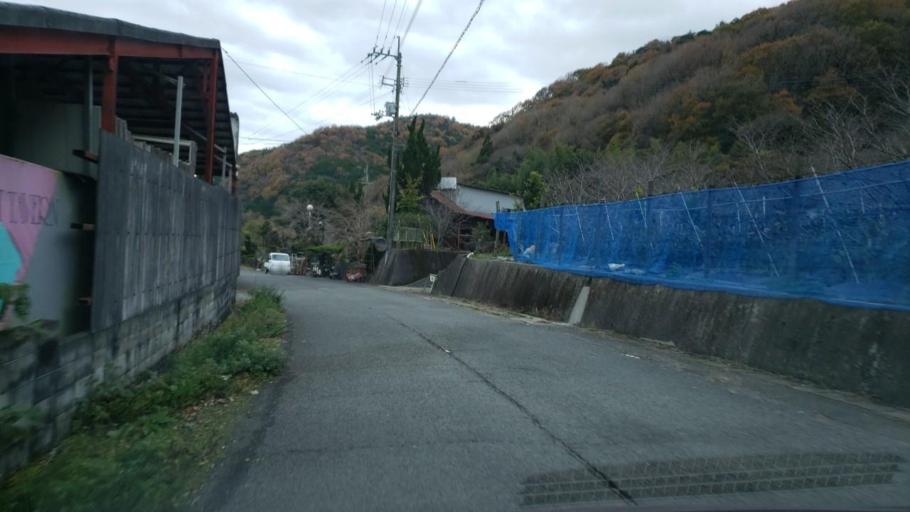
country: JP
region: Tokushima
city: Wakimachi
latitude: 34.1126
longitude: 134.2243
